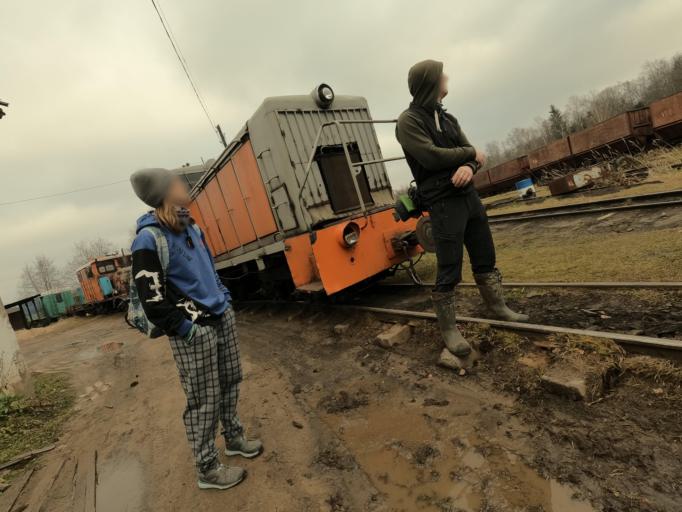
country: RU
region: Leningrad
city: Nurma
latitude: 59.6029
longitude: 31.1997
